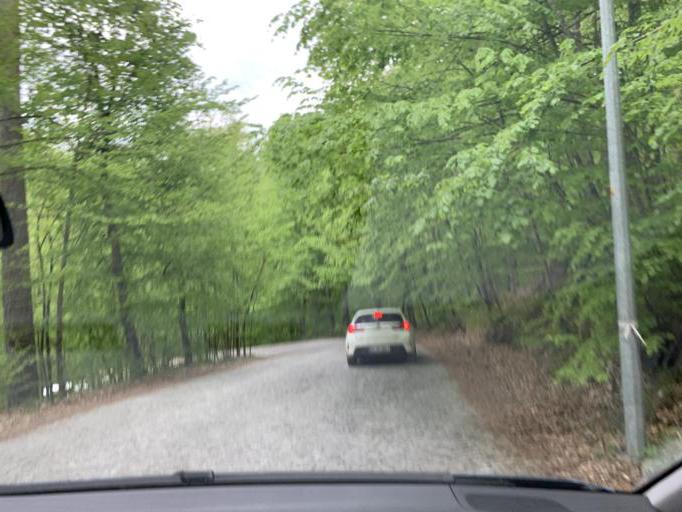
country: TR
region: Zonguldak
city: Egerci
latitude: 40.9406
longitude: 31.7449
